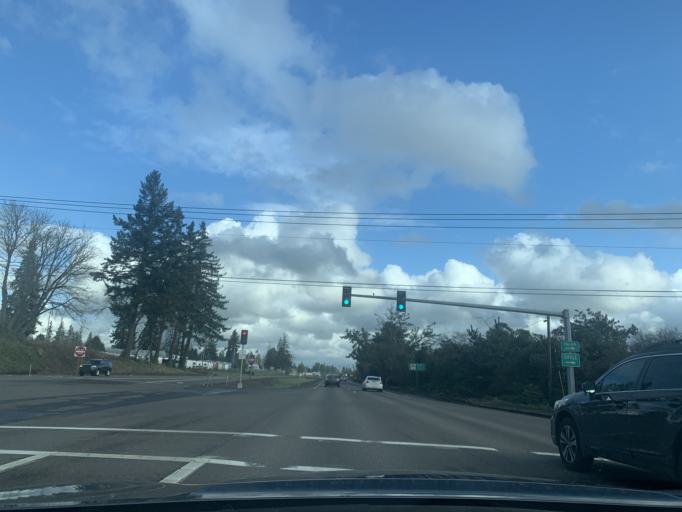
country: US
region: Oregon
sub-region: Washington County
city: King City
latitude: 45.3843
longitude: -122.8175
